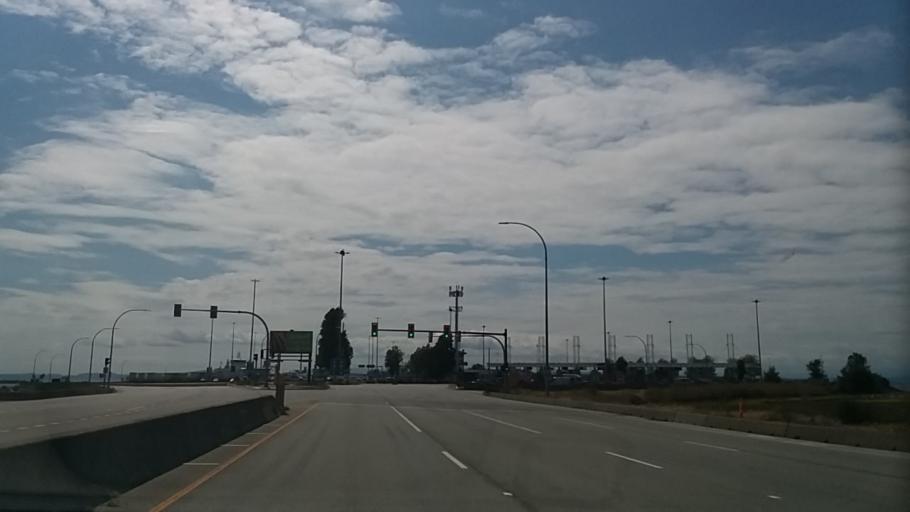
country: US
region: Washington
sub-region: Whatcom County
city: Point Roberts
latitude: 49.0119
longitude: -123.1225
